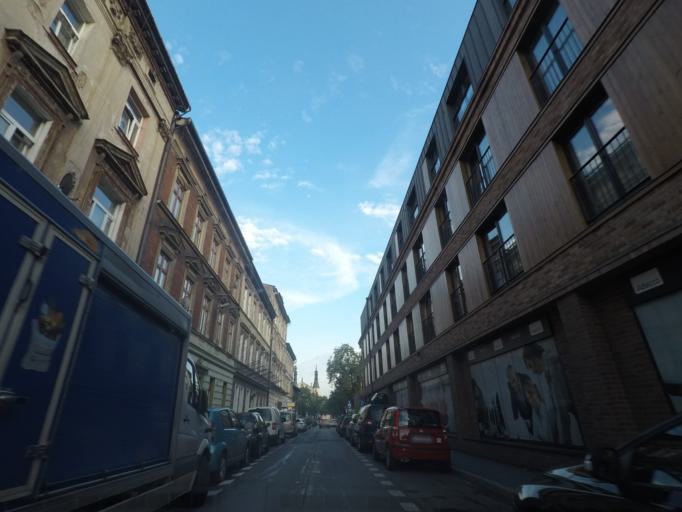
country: PL
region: Lesser Poland Voivodeship
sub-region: Krakow
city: Krakow
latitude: 50.0645
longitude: 19.9502
